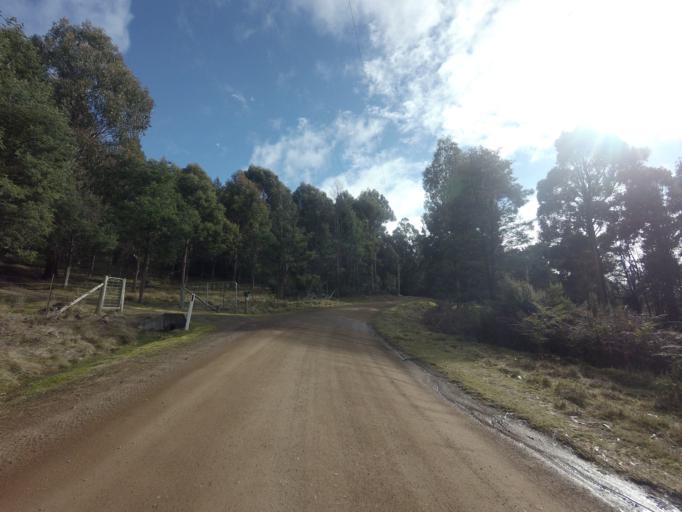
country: AU
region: Tasmania
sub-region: Derwent Valley
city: New Norfolk
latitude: -42.7877
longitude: 146.9177
